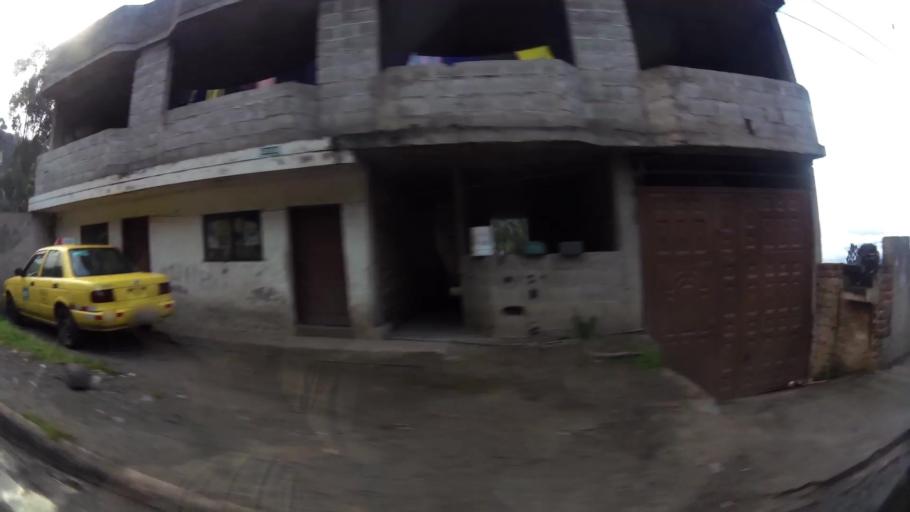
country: EC
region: Pichincha
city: Quito
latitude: -0.1188
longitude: -78.5145
